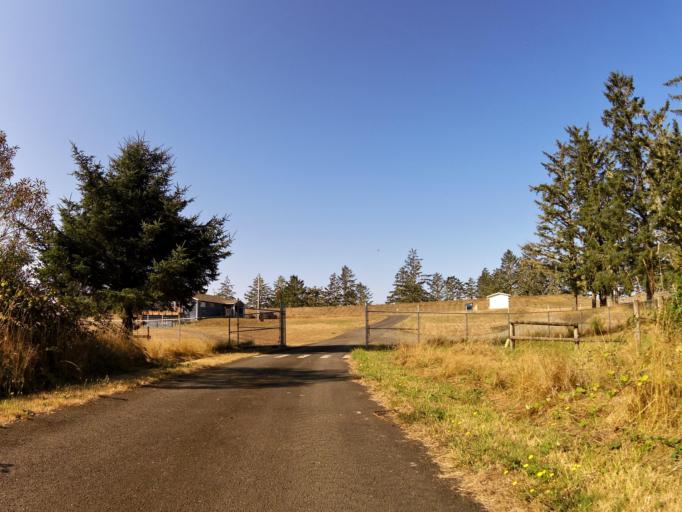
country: US
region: Oregon
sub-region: Clatsop County
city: Warrenton
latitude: 46.1177
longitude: -123.9272
